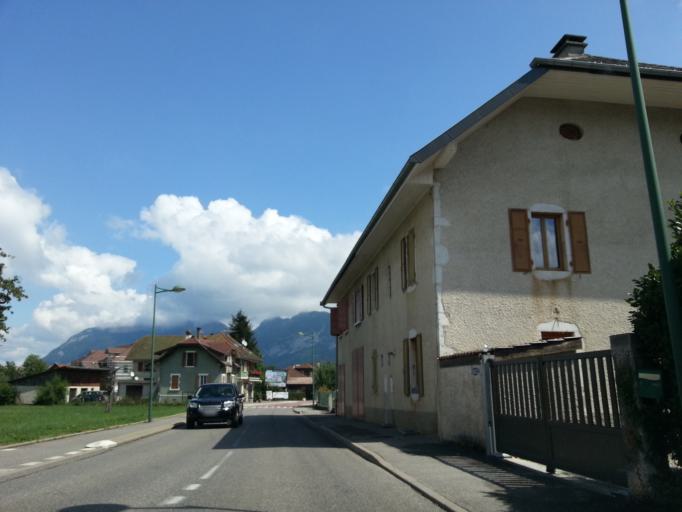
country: FR
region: Rhone-Alpes
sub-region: Departement de la Haute-Savoie
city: Saint-Jorioz
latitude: 45.8309
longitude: 6.1603
